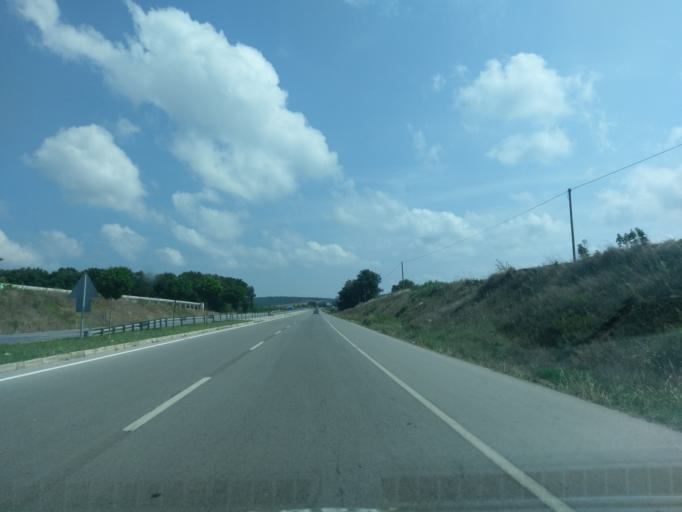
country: TR
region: Samsun
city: Bafra
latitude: 41.6030
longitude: 35.8219
